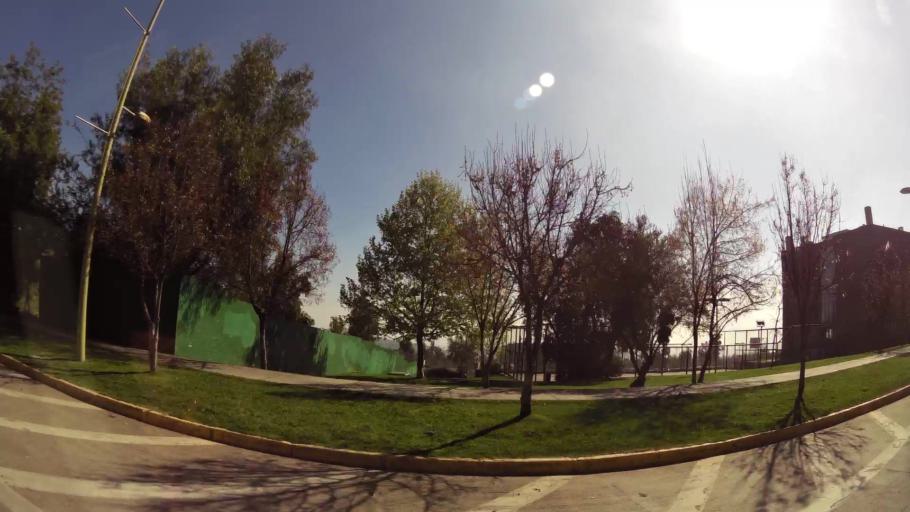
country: CL
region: Santiago Metropolitan
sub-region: Provincia de Santiago
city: Villa Presidente Frei, Nunoa, Santiago, Chile
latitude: -33.4007
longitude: -70.5065
